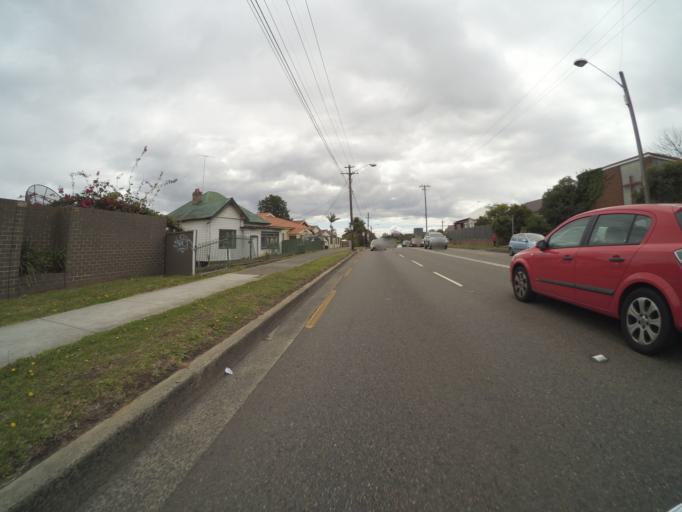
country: AU
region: New South Wales
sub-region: Kogarah
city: Hurstville Grove
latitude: -33.9755
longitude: 151.1029
